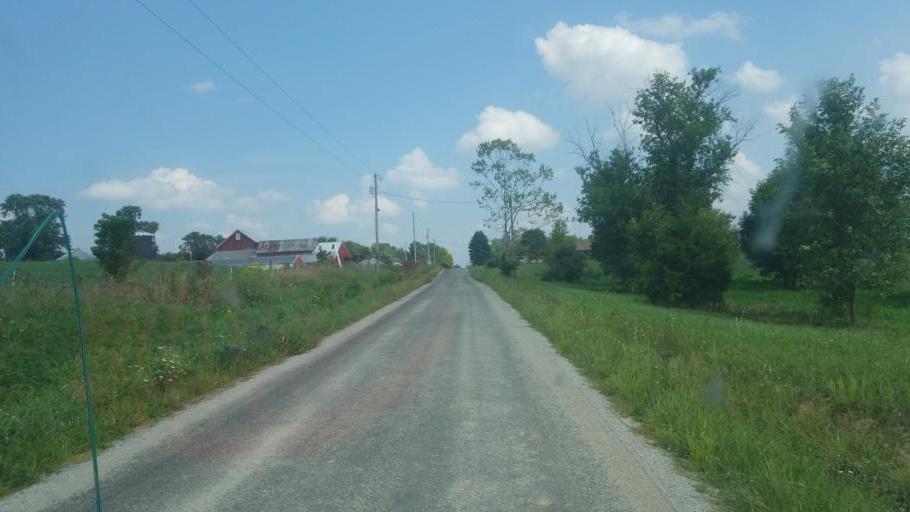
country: US
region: Ohio
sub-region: Huron County
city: New London
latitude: 41.0494
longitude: -82.3603
